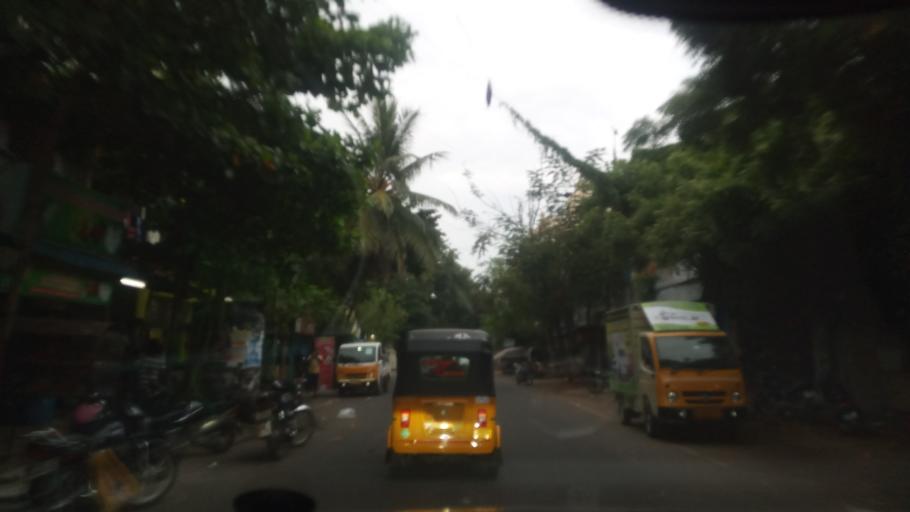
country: IN
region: Tamil Nadu
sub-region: Chennai
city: Chetput
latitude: 13.0419
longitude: 80.2138
